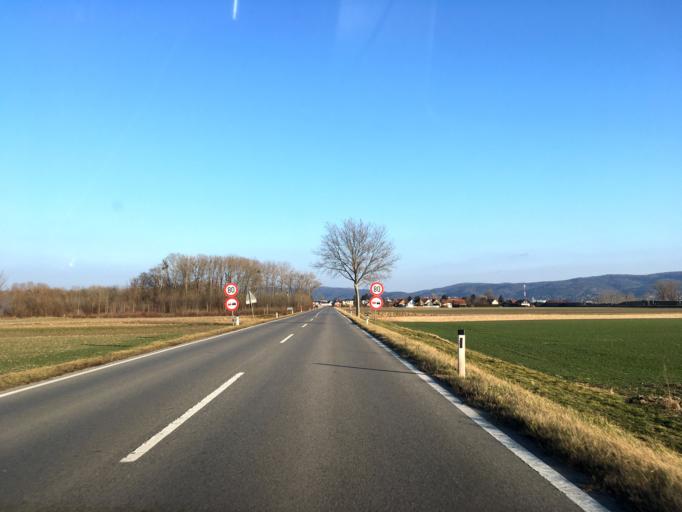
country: AT
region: Lower Austria
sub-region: Politischer Bezirk Tulln
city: Konigstetten
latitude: 48.3315
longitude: 16.1385
